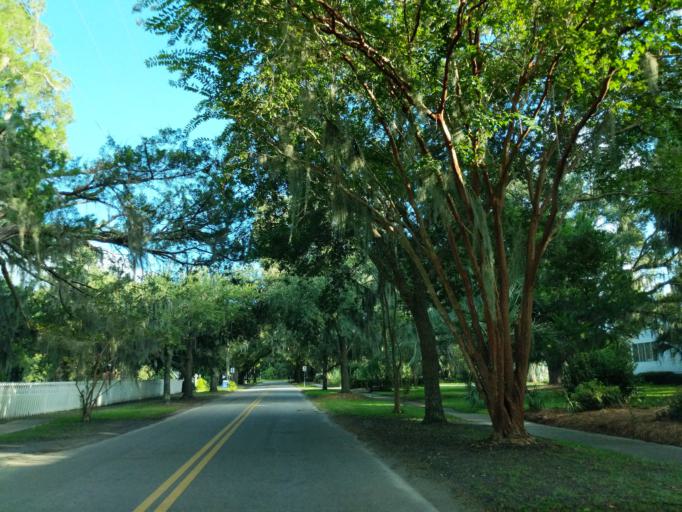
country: US
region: South Carolina
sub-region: Charleston County
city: Awendaw
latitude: 33.0823
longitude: -79.4591
